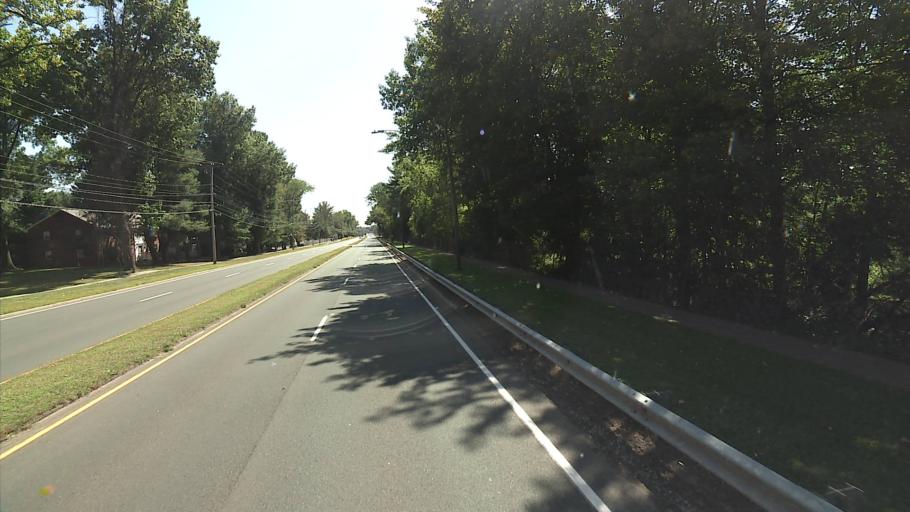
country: US
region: Connecticut
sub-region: Hartford County
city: Windsor
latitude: 41.8276
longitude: -72.6561
